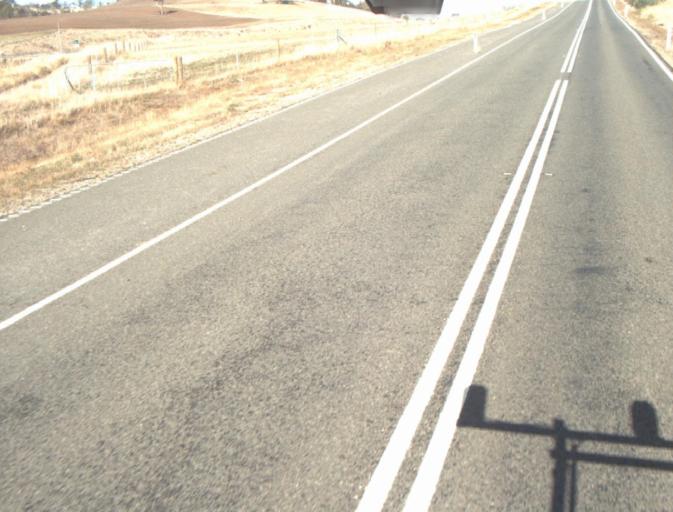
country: AU
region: Tasmania
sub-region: Launceston
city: Mayfield
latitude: -41.3514
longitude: 147.0991
